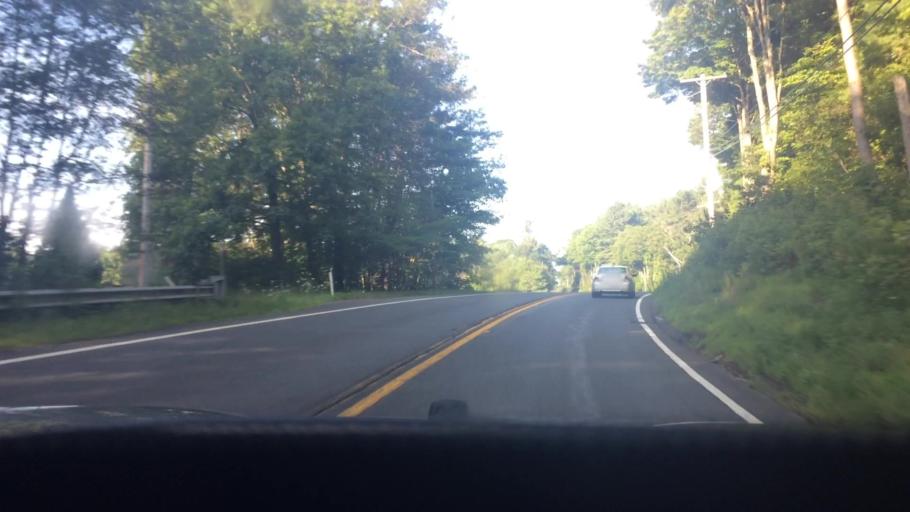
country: US
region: Massachusetts
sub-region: Franklin County
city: Erving
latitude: 42.5938
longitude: -72.4427
